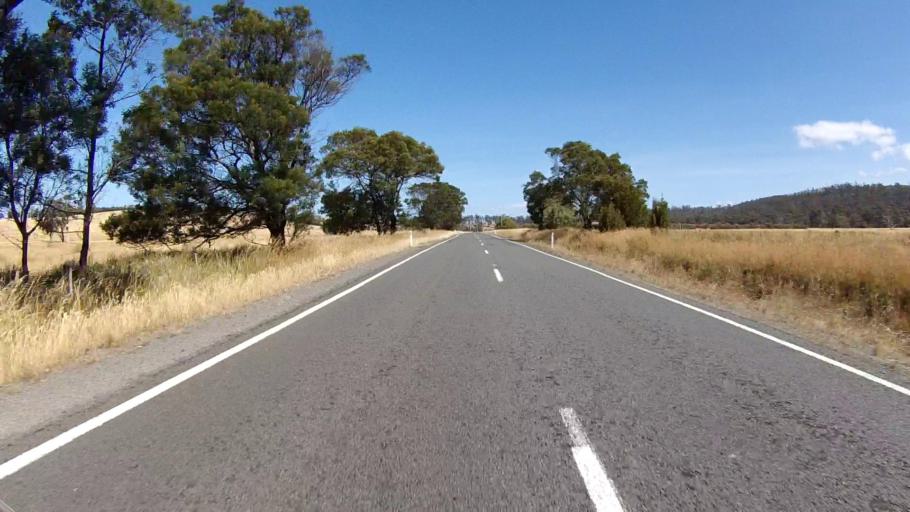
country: AU
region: Tasmania
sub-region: Sorell
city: Sorell
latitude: -42.4557
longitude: 147.9285
